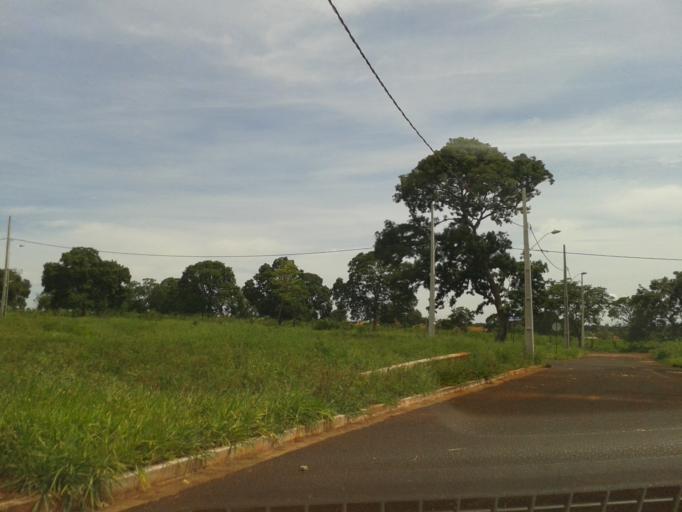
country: BR
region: Minas Gerais
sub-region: Santa Vitoria
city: Santa Vitoria
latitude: -18.8411
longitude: -50.1341
